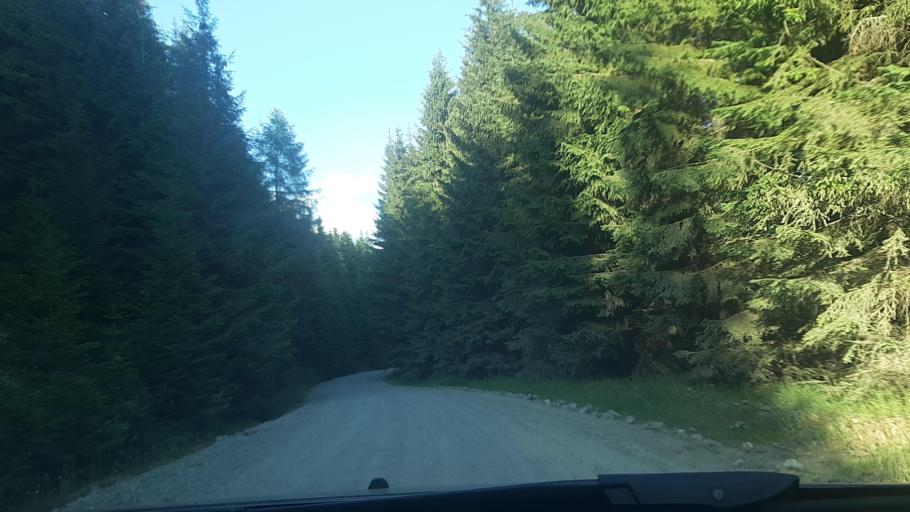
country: RO
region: Alba
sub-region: Comuna Sugag
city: Sugag
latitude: 45.5815
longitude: 23.6106
